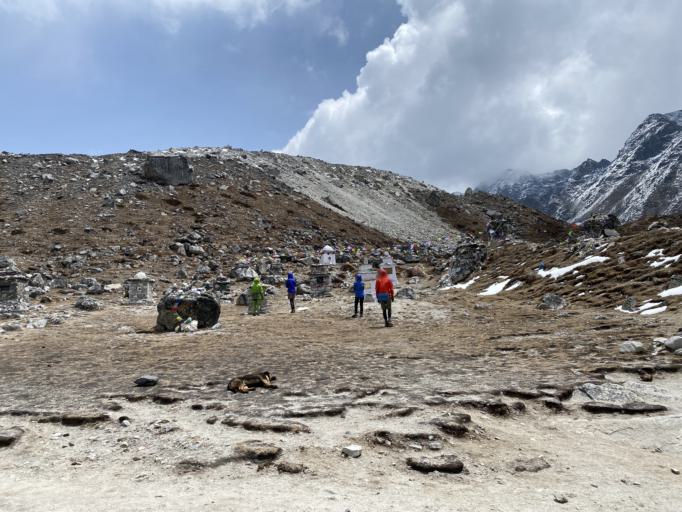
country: NP
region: Eastern Region
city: Lobujya
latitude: 27.9311
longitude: 86.8045
